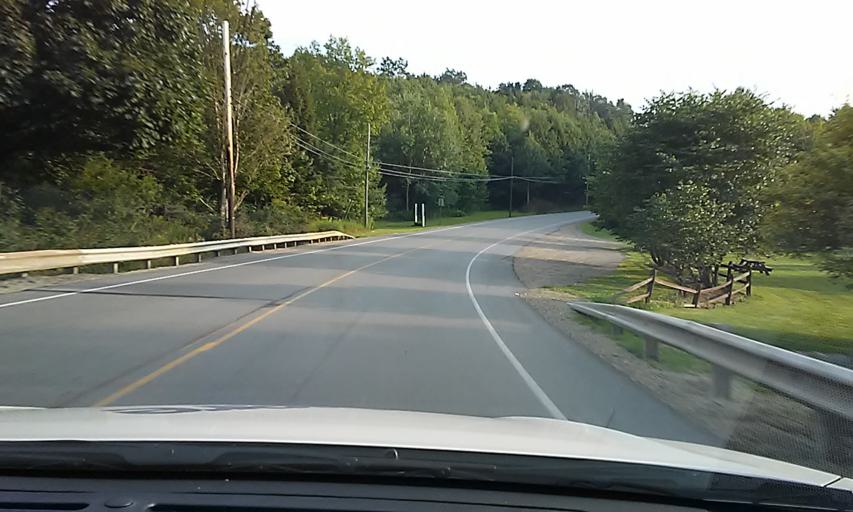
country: US
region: Pennsylvania
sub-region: McKean County
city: Kane
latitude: 41.6532
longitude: -78.8110
